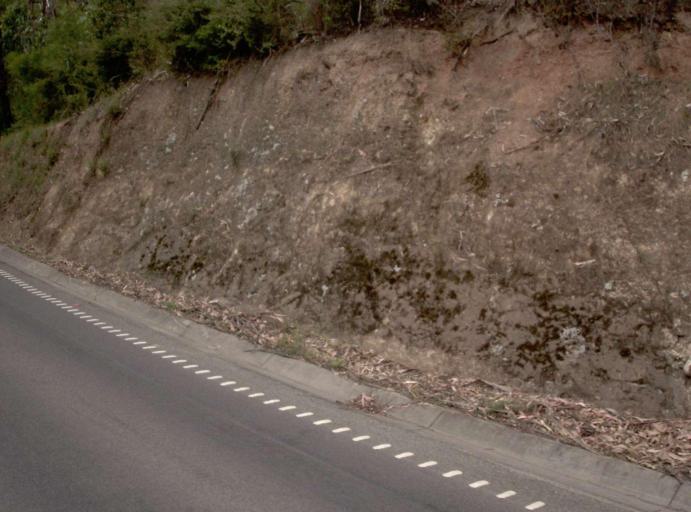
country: AU
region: Victoria
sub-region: Yarra Ranges
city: Yarra Glen
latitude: -37.5320
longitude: 145.4144
